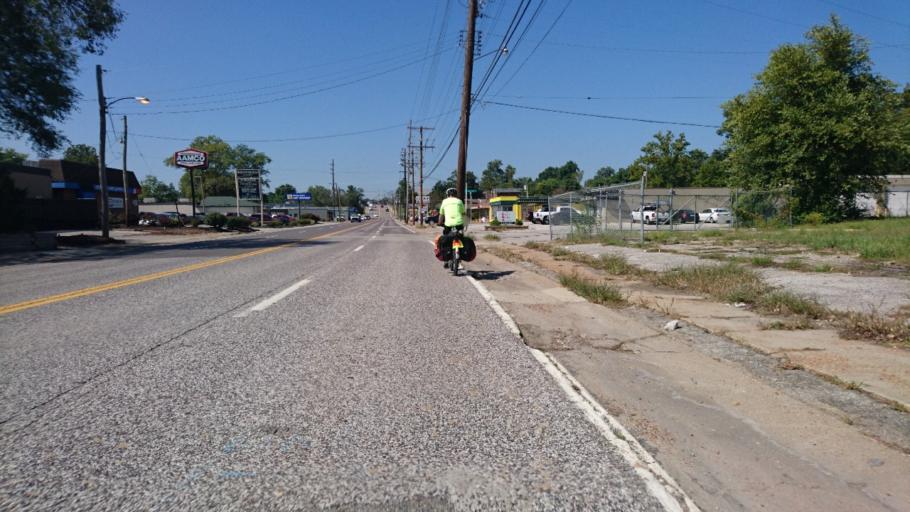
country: US
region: Missouri
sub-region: Saint Louis County
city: Brentwood
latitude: 38.6122
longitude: -90.3423
